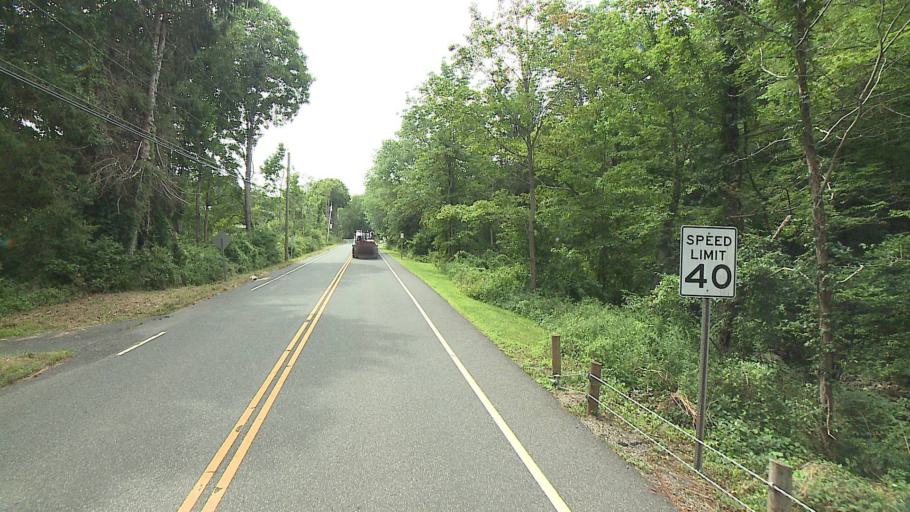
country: US
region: Connecticut
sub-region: Litchfield County
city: Woodbury
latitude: 41.5950
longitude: -73.2578
